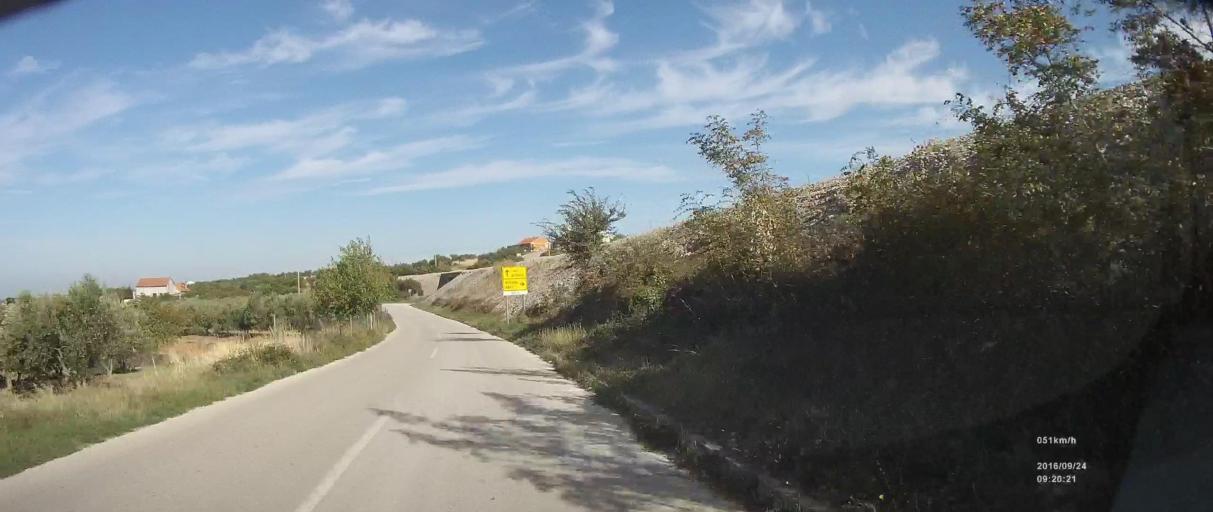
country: HR
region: Zadarska
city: Polaca
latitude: 44.0679
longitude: 15.4977
